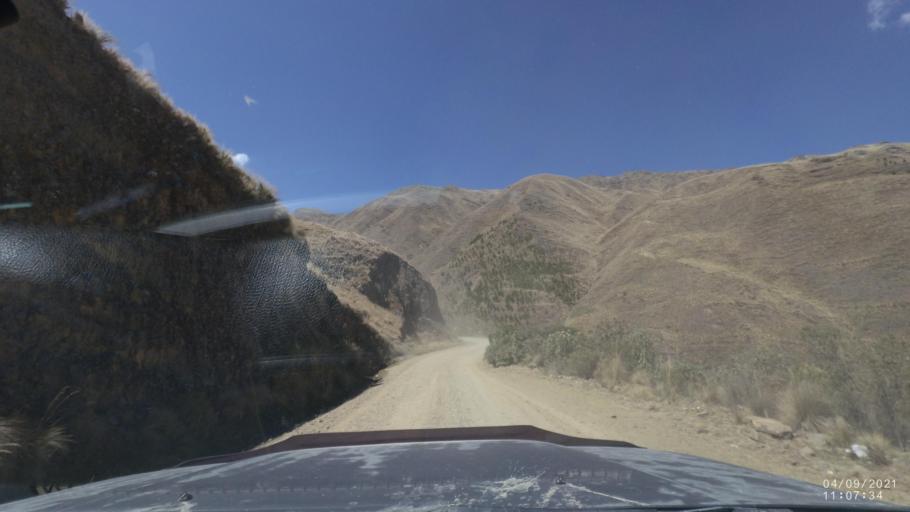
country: BO
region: Cochabamba
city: Sipe Sipe
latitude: -17.2805
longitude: -66.4752
